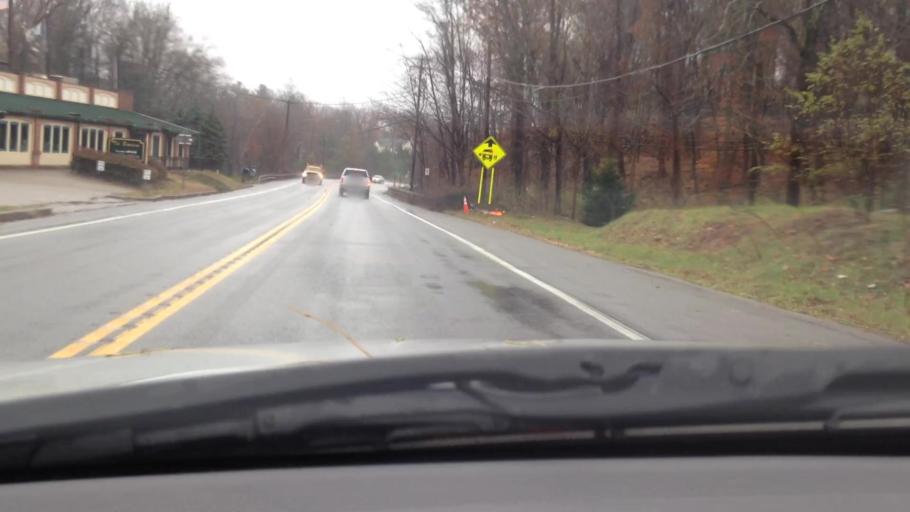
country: US
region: New York
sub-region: Orange County
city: Highland Falls
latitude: 41.3406
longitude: -73.9248
